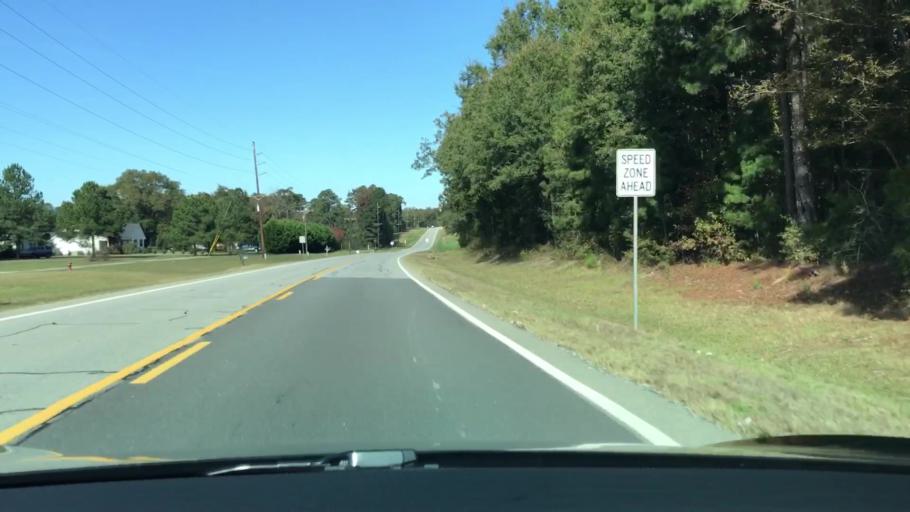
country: US
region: Georgia
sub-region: Warren County
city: Warrenton
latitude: 33.3928
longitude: -82.6486
